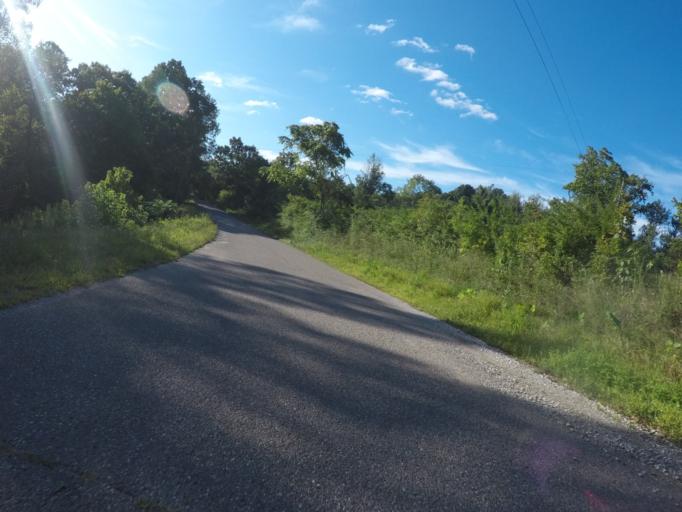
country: US
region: West Virginia
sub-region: Cabell County
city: Huntington
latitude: 38.4732
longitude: -82.4586
